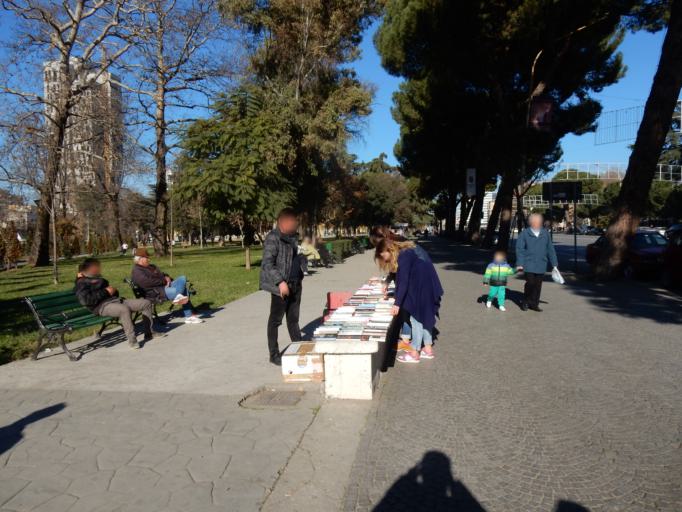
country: AL
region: Tirane
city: Tirana
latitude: 41.3245
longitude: 19.8190
